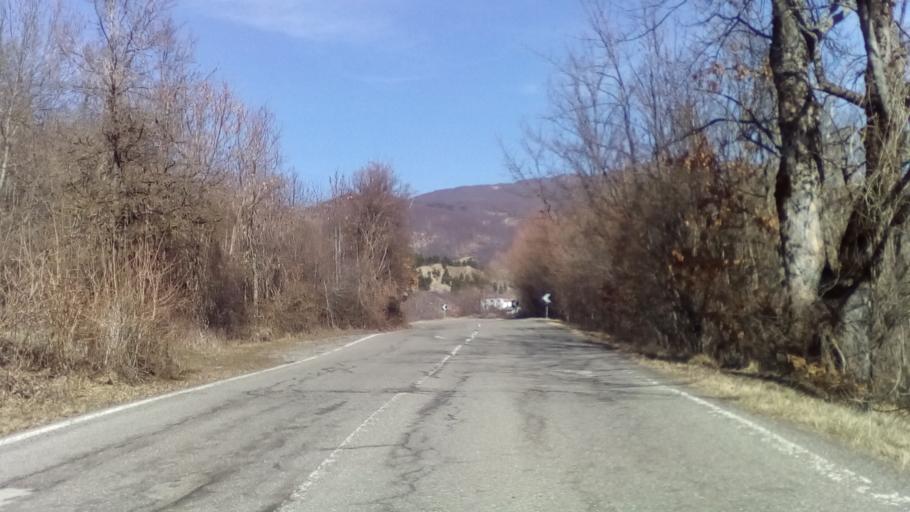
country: IT
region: Emilia-Romagna
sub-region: Provincia di Modena
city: Riolunato
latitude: 44.2425
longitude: 10.6337
